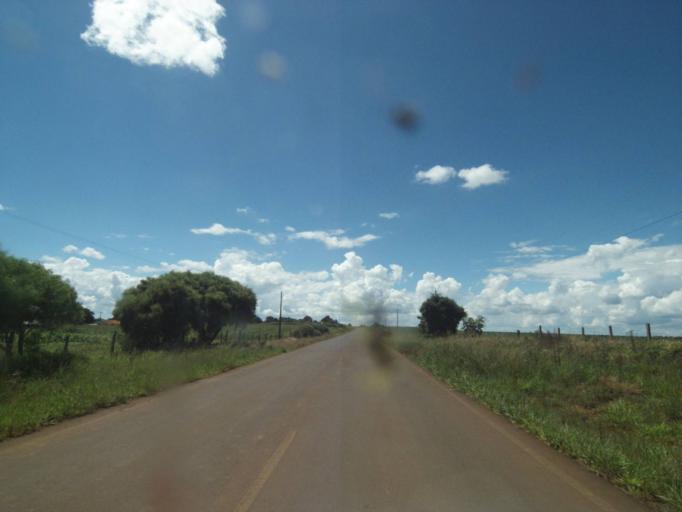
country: BR
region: Parana
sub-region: Pinhao
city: Pinhao
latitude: -25.8187
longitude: -52.0420
